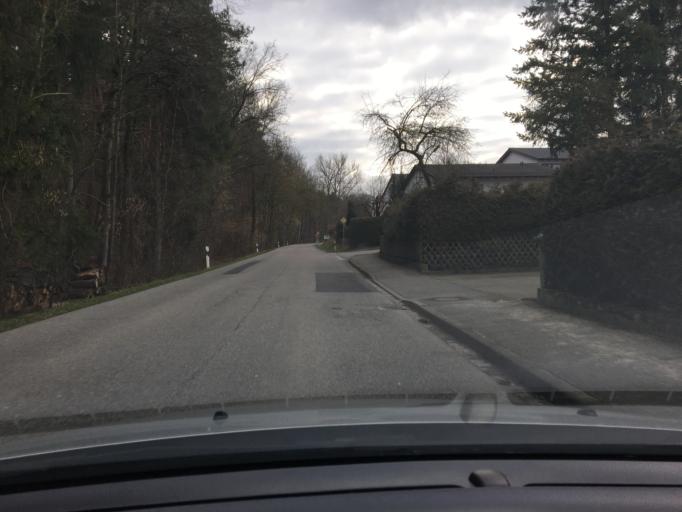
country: DE
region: Bavaria
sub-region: Lower Bavaria
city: Kumhausen
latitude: 48.5098
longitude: 12.1561
